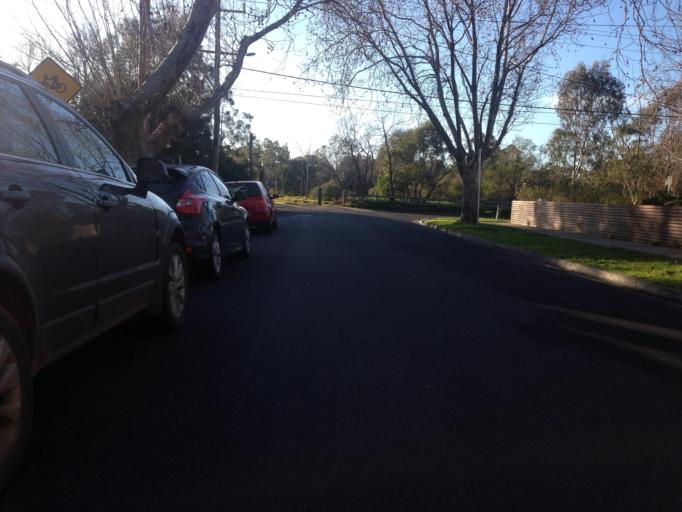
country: AU
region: Victoria
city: Alphington
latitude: -37.7750
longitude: 145.0314
